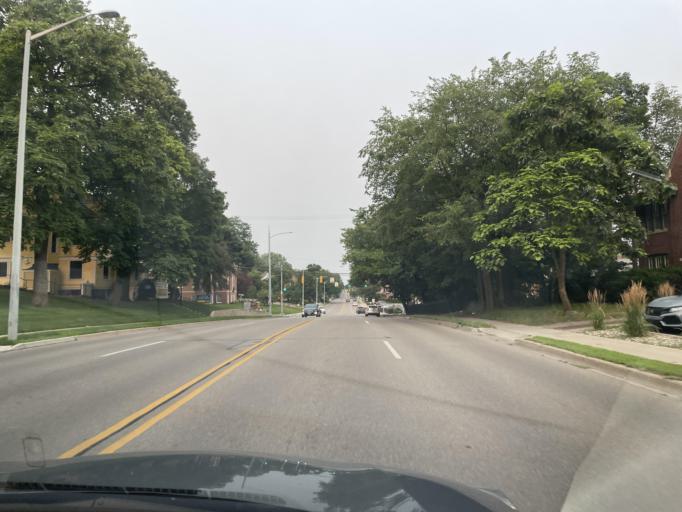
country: US
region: Michigan
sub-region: Kent County
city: Grand Rapids
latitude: 42.9630
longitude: -85.6580
